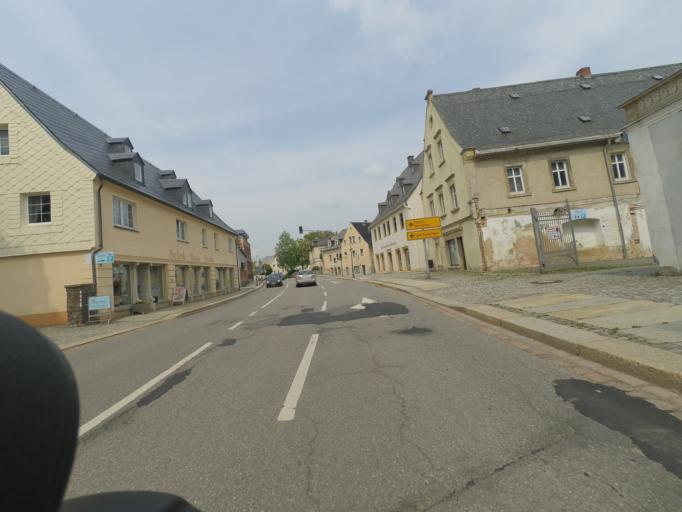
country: DE
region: Saxony
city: Olbernhau
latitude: 50.6616
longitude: 13.3348
